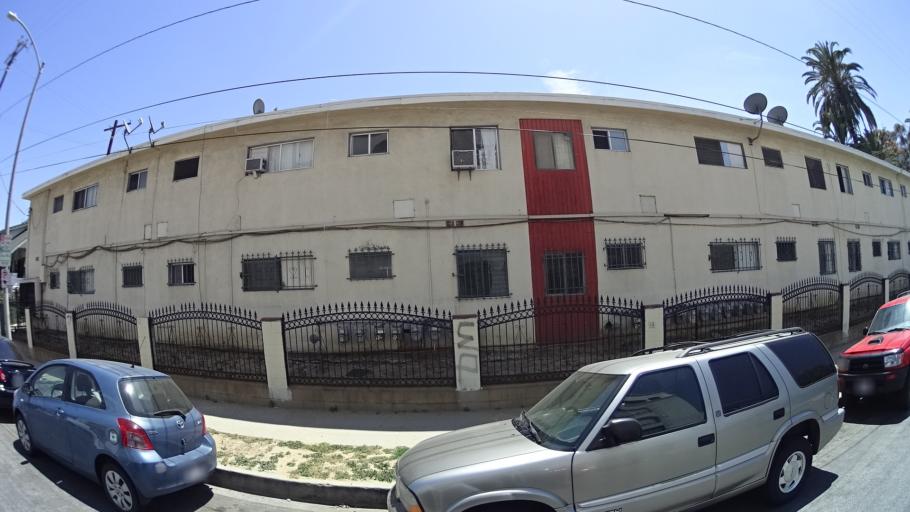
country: US
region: California
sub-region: Los Angeles County
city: Echo Park
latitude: 34.0760
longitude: -118.2603
